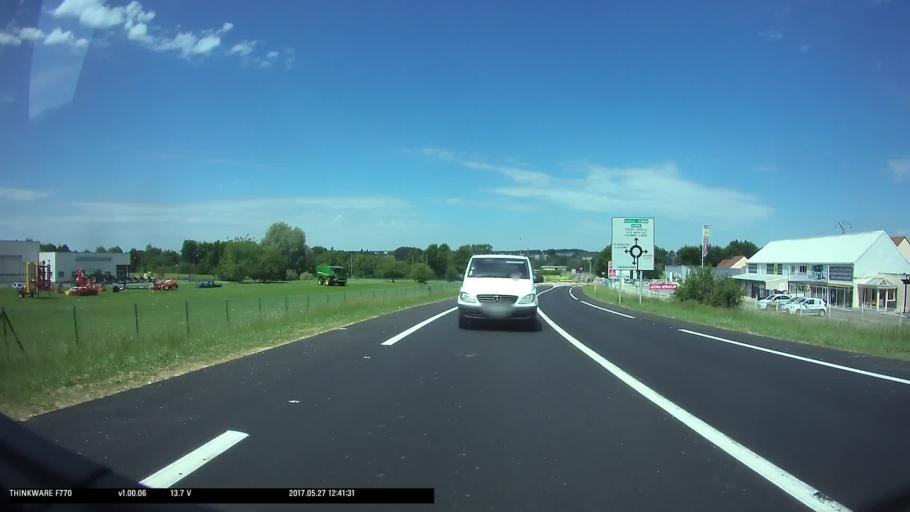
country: FR
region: Haute-Normandie
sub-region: Departement de l'Eure
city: Gisors
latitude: 49.2697
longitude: 1.7757
